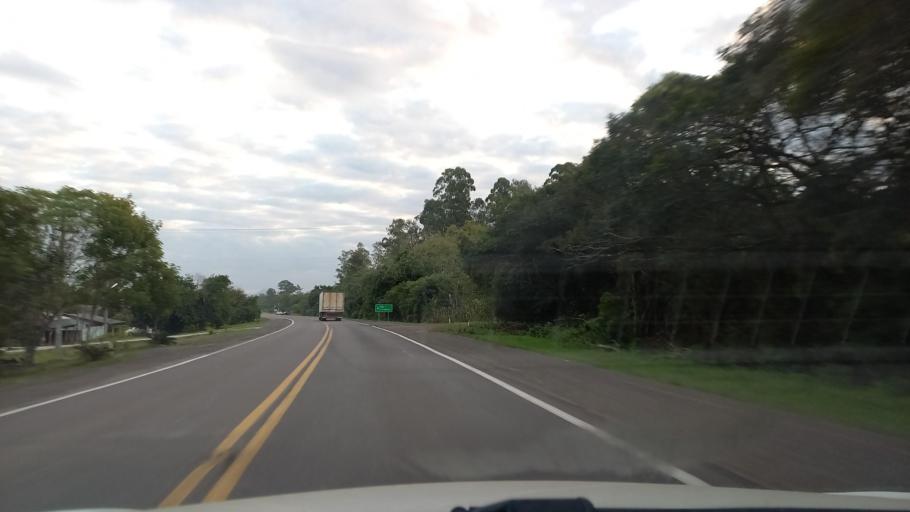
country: BR
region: Rio Grande do Sul
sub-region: Santa Cruz Do Sul
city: Santa Cruz do Sul
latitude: -29.7010
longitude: -52.5300
